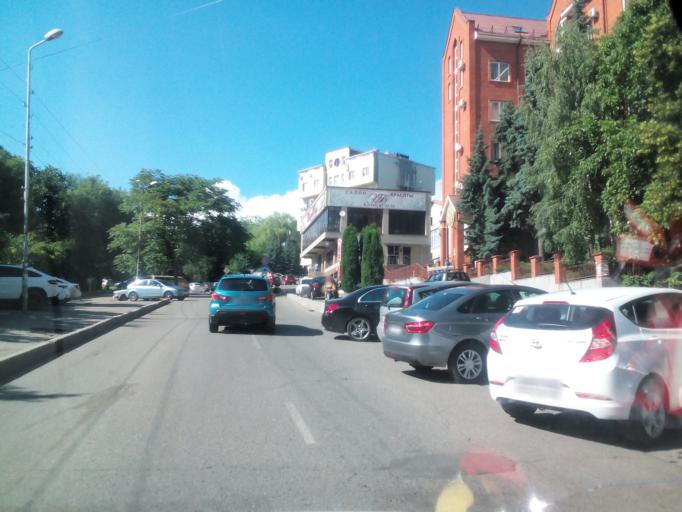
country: RU
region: Stavropol'skiy
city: Pyatigorsk
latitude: 44.0474
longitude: 43.0686
